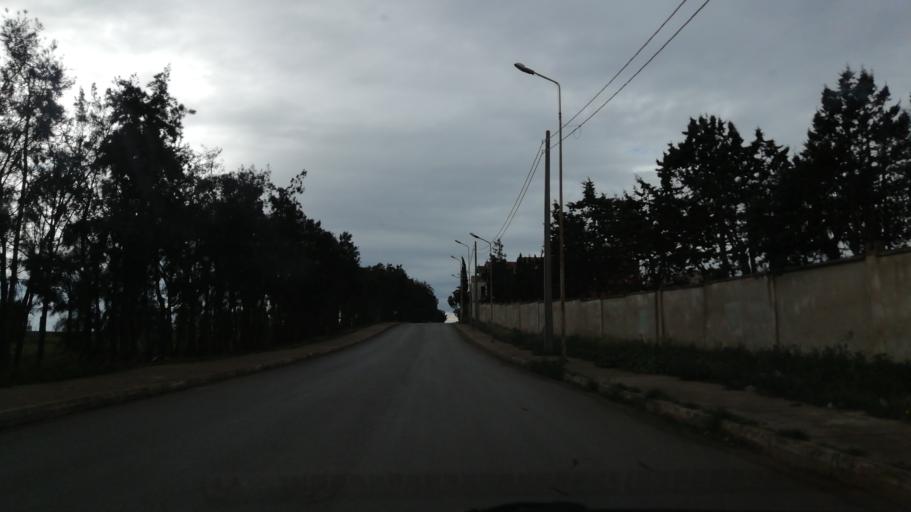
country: DZ
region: Oran
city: Oran
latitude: 35.6962
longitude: -0.5978
